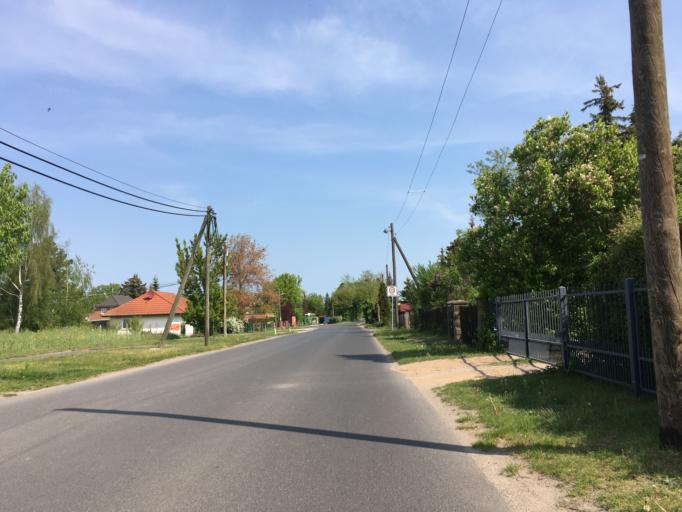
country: DE
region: Brandenburg
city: Altlandsberg
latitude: 52.5789
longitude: 13.7251
